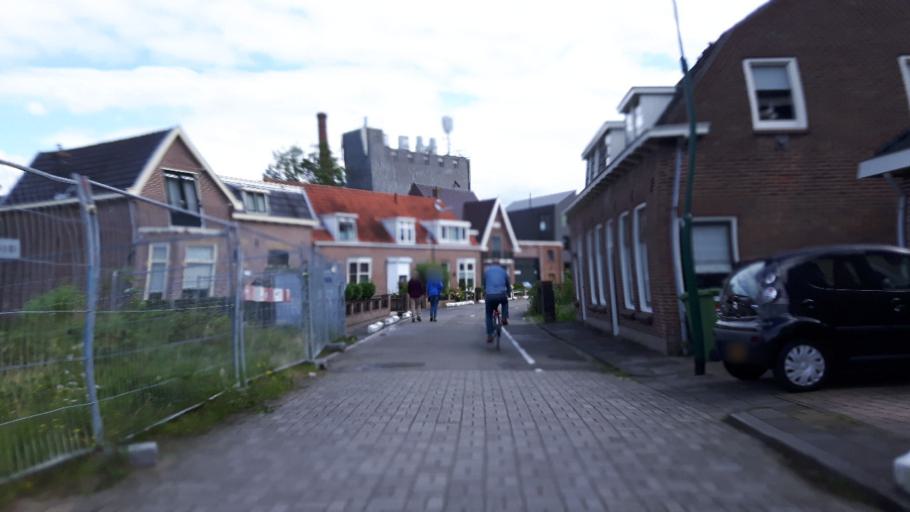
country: NL
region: Utrecht
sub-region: Gemeente IJsselstein
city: IJsselstein
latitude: 52.0219
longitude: 5.0454
